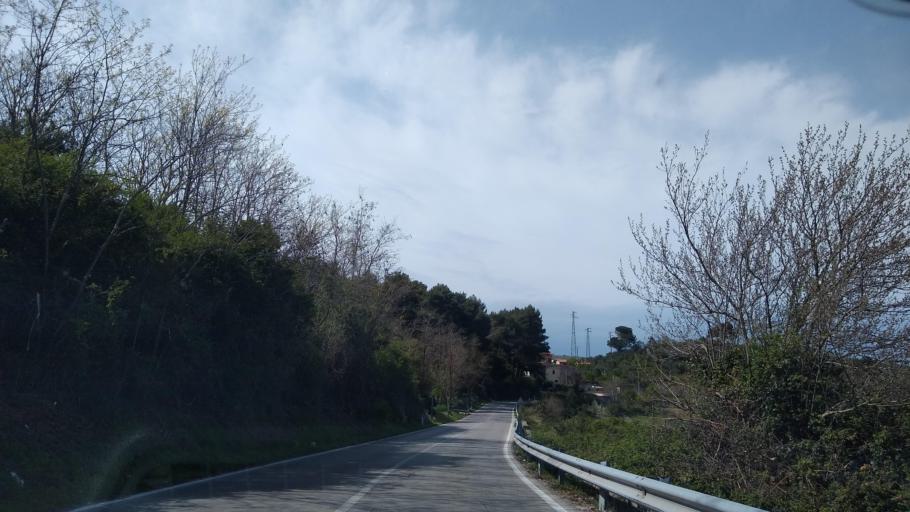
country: IT
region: Sicily
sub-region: Palermo
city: Pioppo
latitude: 38.0398
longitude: 13.2035
